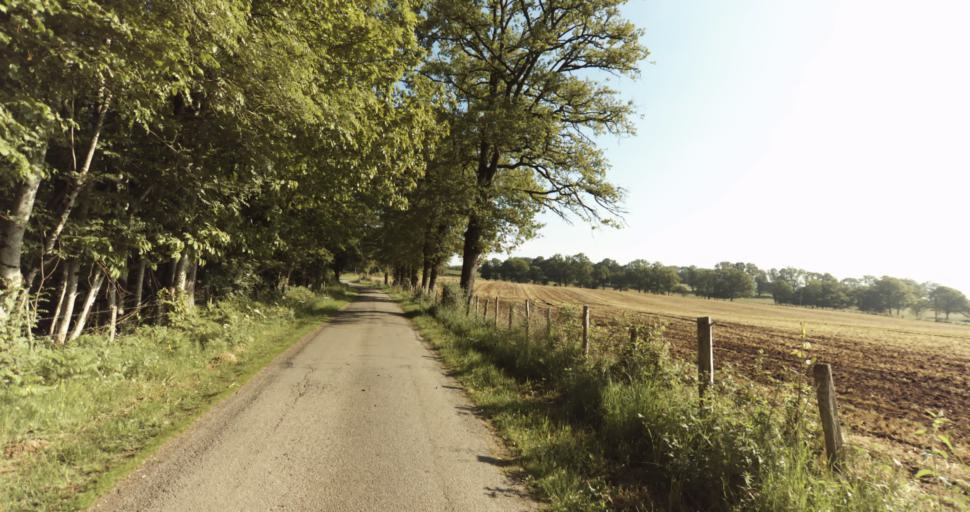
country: FR
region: Limousin
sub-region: Departement de la Haute-Vienne
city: Solignac
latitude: 45.7323
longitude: 1.2604
